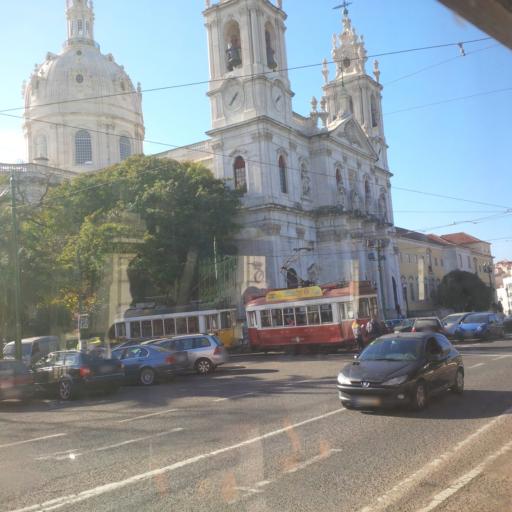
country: PT
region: Lisbon
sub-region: Lisbon
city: Lisbon
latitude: 38.7135
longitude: -9.1596
